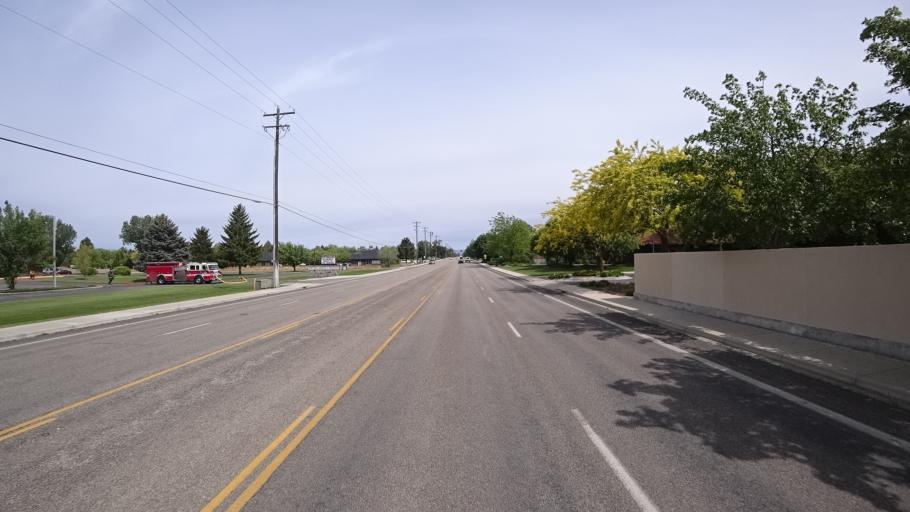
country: US
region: Idaho
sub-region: Ada County
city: Meridian
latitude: 43.5782
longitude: -116.3142
